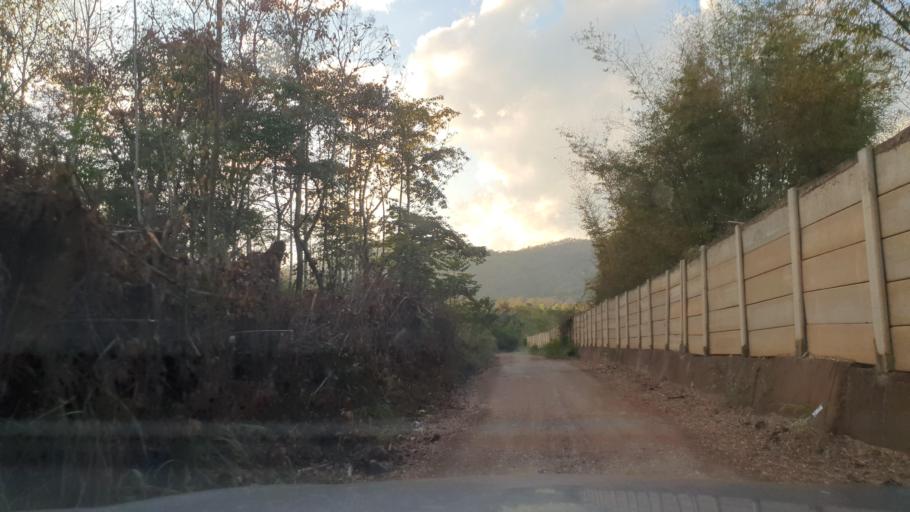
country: TH
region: Chiang Mai
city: Hang Dong
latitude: 18.7344
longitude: 98.8843
